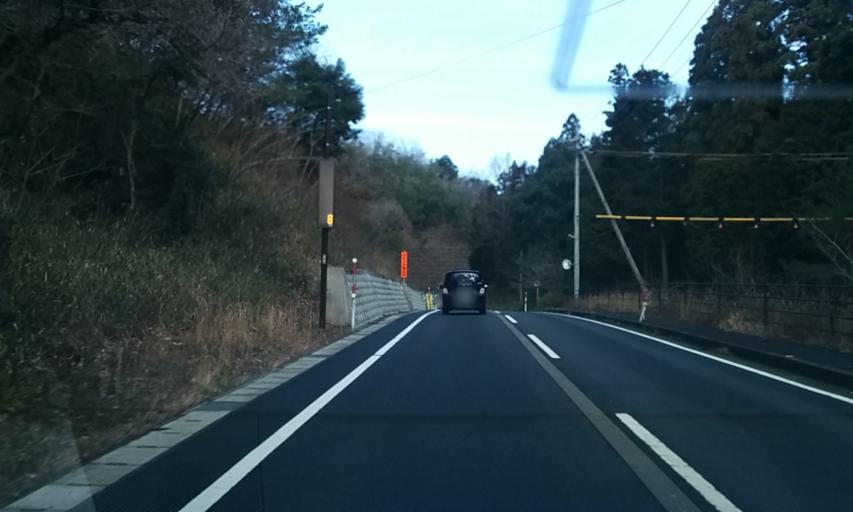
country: JP
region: Kyoto
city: Miyazu
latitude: 35.5807
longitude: 135.1180
